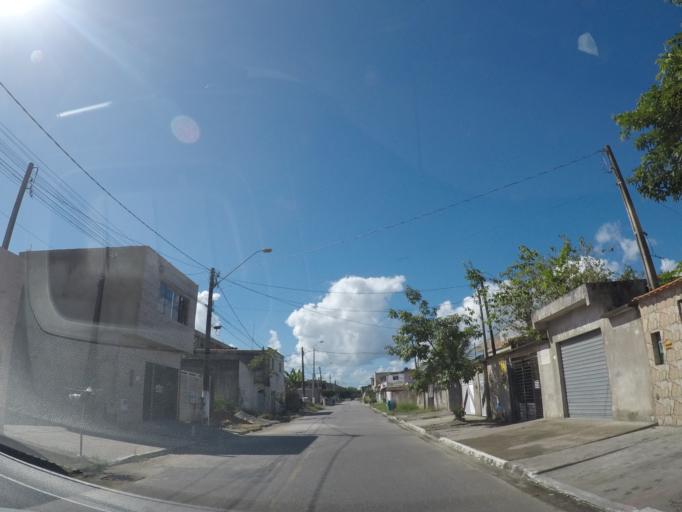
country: BR
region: Sao Paulo
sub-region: Praia Grande
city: Praia Grande
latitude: -24.0220
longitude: -46.5076
